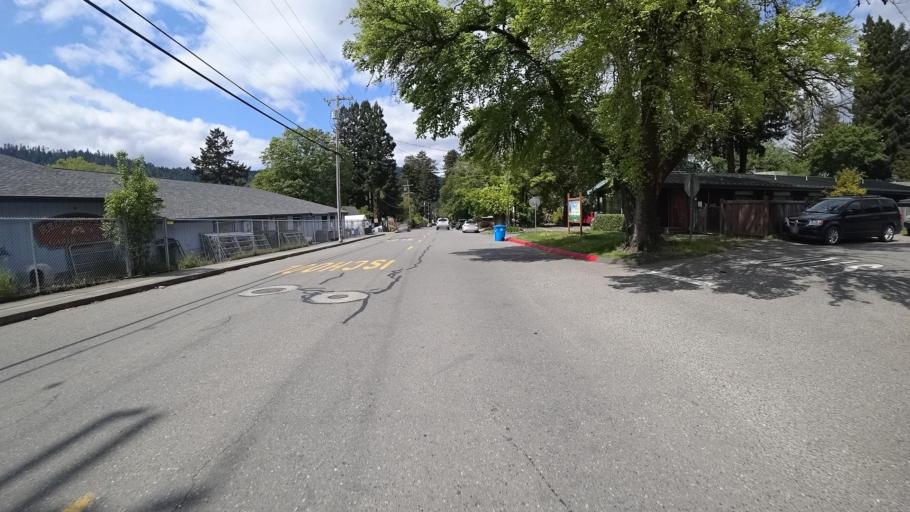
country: US
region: California
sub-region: Humboldt County
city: Redway
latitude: 40.1209
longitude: -123.8261
